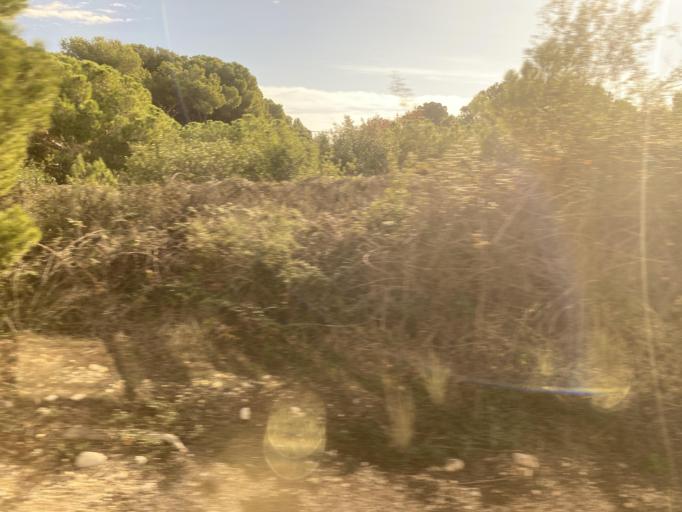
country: ES
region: Catalonia
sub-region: Provincia de Barcelona
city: Sitges
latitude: 41.2302
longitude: 1.7849
